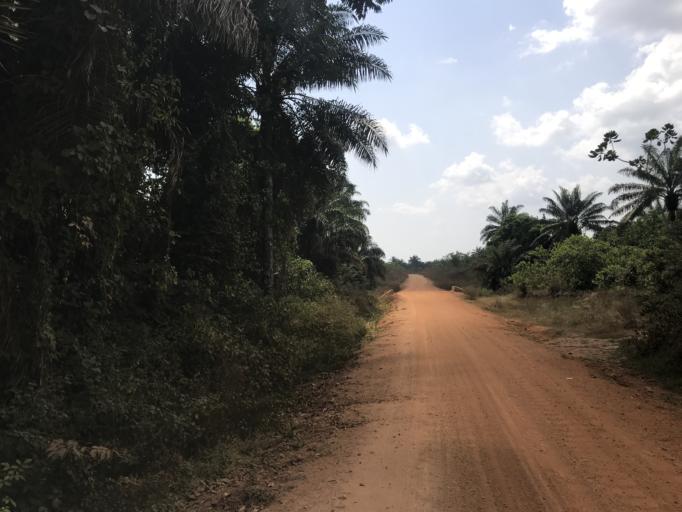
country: NG
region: Osun
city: Ifon
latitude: 7.9773
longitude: 4.5140
